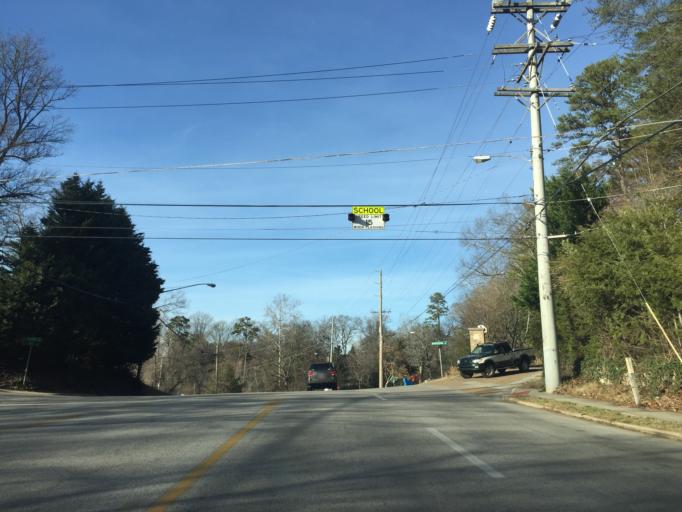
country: US
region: Tennessee
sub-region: Hamilton County
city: Red Bank
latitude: 35.0816
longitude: -85.2899
